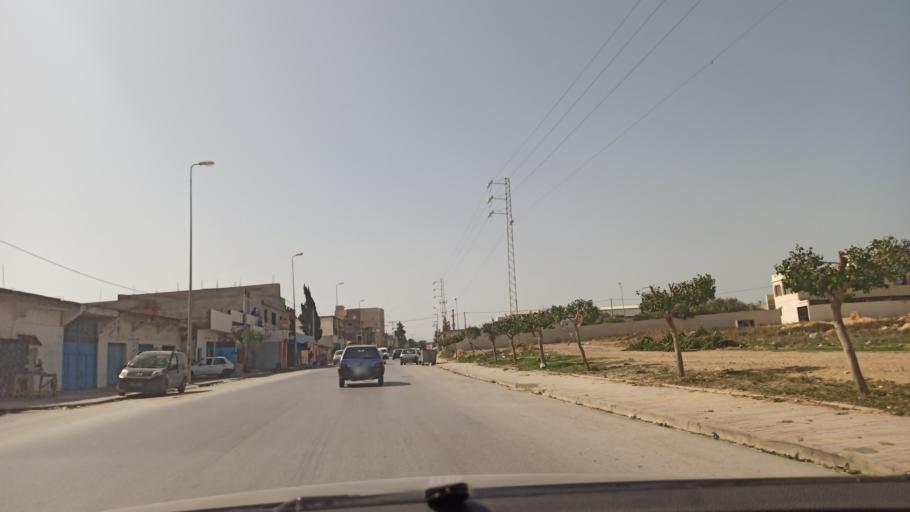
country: TN
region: Manouba
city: Manouba
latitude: 36.7629
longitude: 10.1092
